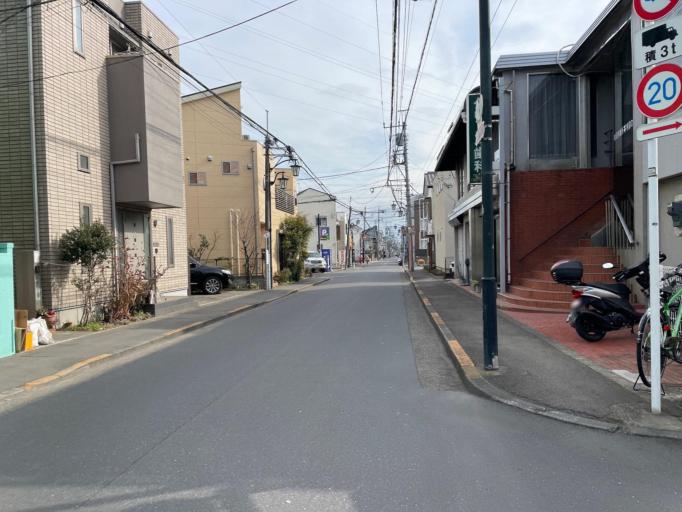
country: JP
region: Tokyo
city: Kamirenjaku
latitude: 35.6995
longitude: 139.5329
